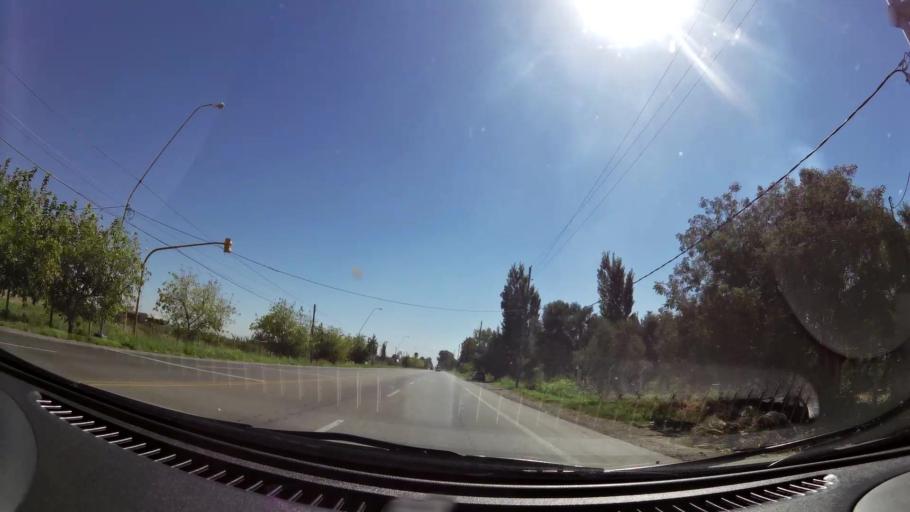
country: AR
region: San Juan
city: Villa Aberastain
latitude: -31.6225
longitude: -68.5511
